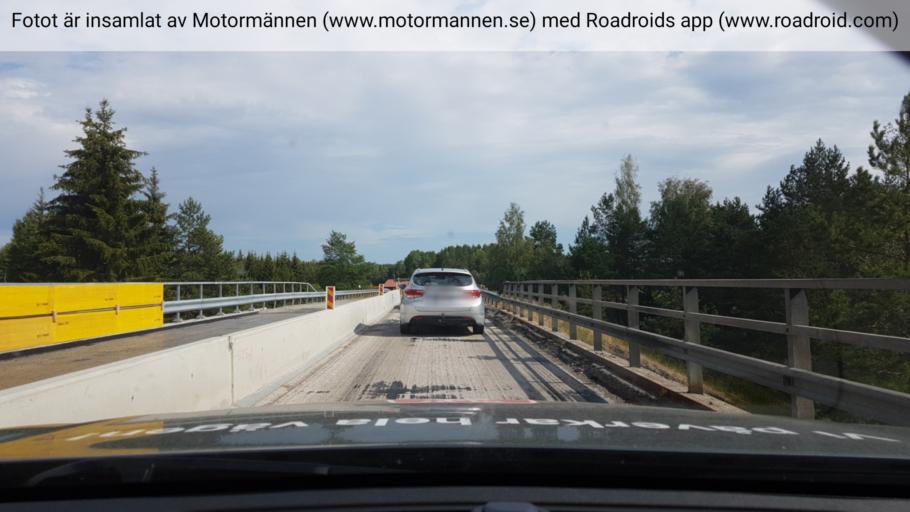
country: SE
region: Uppsala
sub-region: Enkopings Kommun
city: Orsundsbro
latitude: 59.8605
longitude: 17.3706
